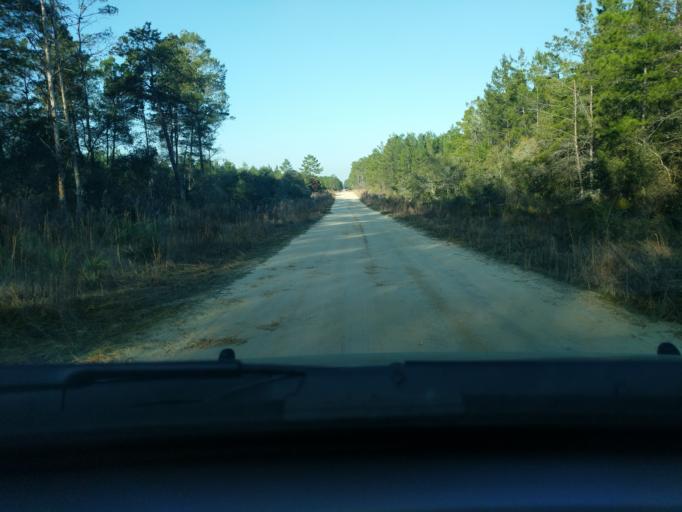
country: US
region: Florida
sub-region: Lake County
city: Astor
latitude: 29.2261
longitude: -81.7762
